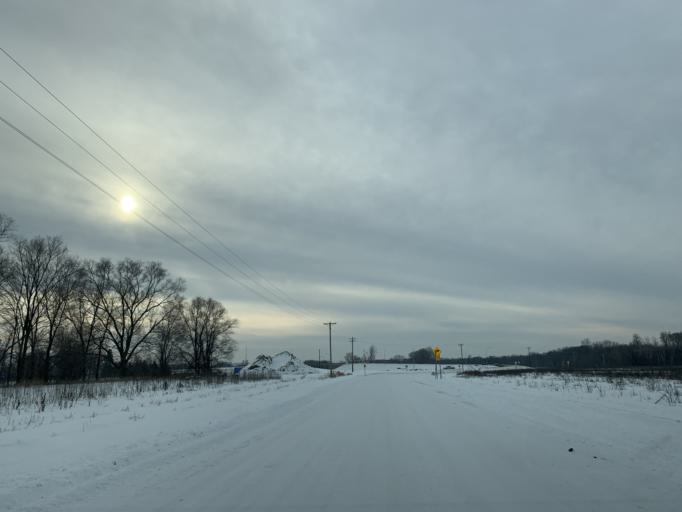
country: US
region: Minnesota
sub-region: Washington County
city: Forest Lake
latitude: 45.2938
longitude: -93.0040
